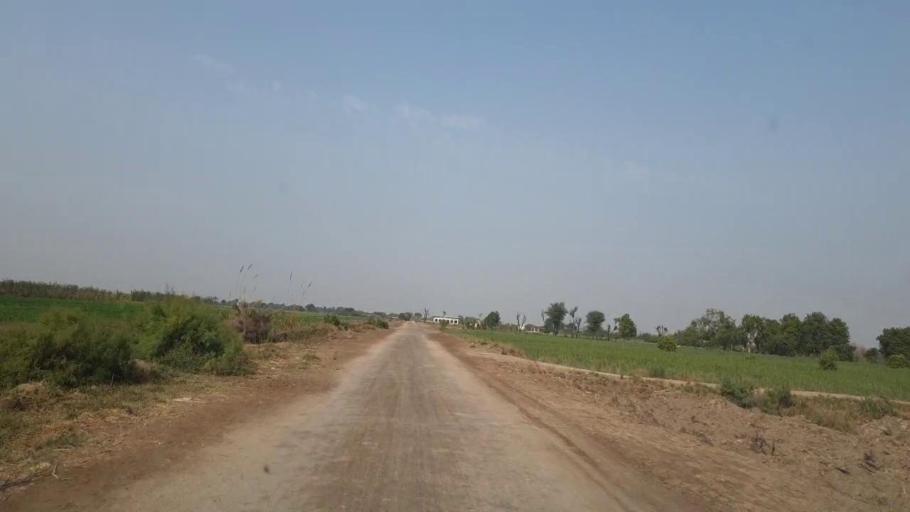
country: PK
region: Sindh
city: Mirpur Khas
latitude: 25.5624
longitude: 69.1524
